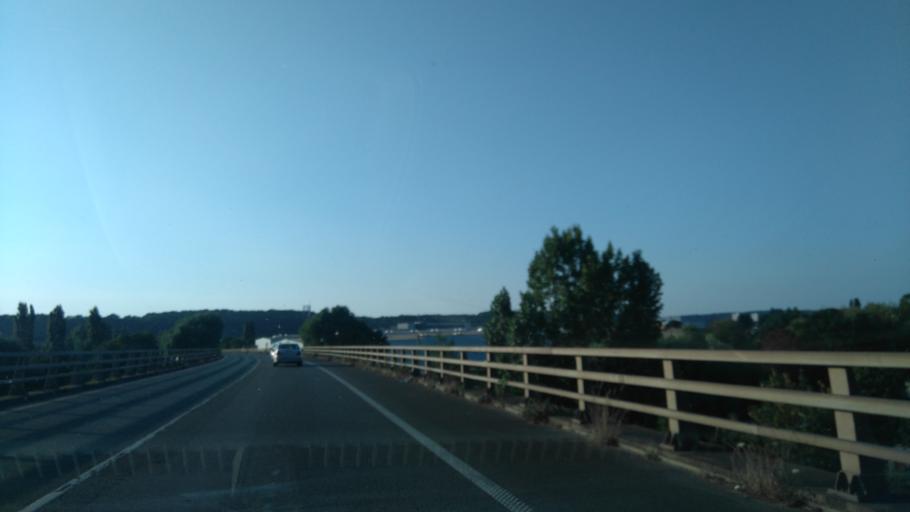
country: FR
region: Picardie
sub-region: Departement de l'Oise
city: Montataire
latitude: 49.2514
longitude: 2.4575
